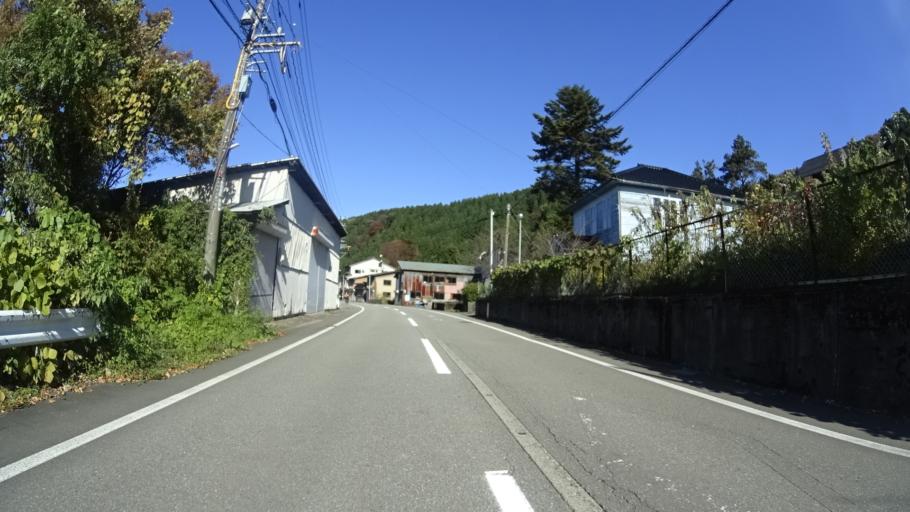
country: JP
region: Ishikawa
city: Tsurugi-asahimachi
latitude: 36.4354
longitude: 136.6340
